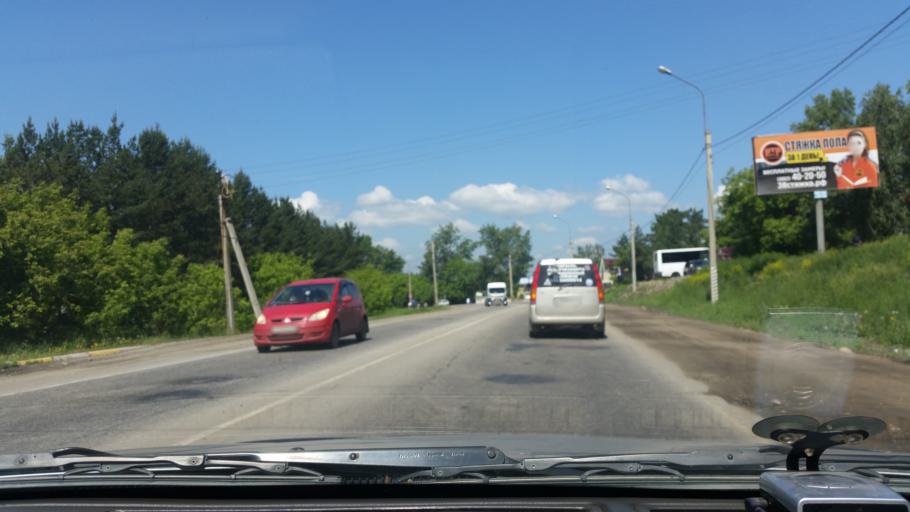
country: RU
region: Irkutsk
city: Smolenshchina
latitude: 52.2606
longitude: 104.1954
